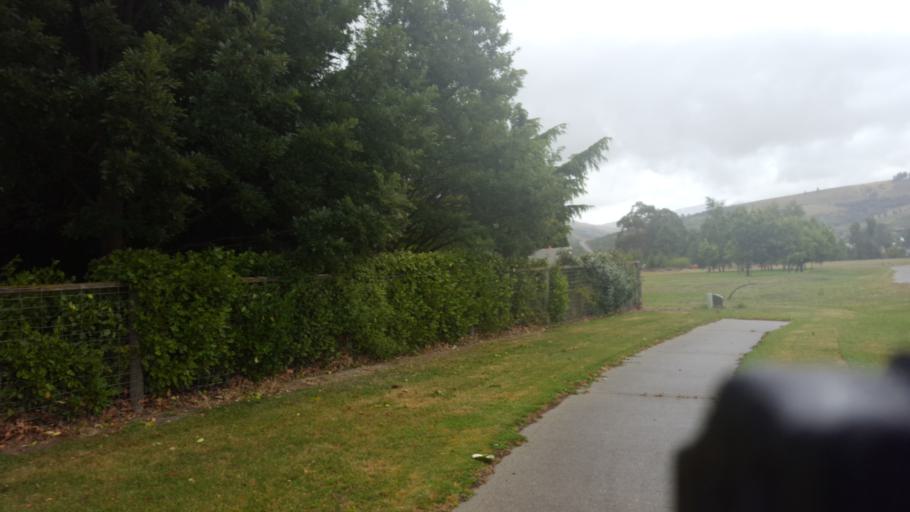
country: NZ
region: Otago
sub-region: Queenstown-Lakes District
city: Wanaka
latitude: -45.1951
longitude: 169.3156
